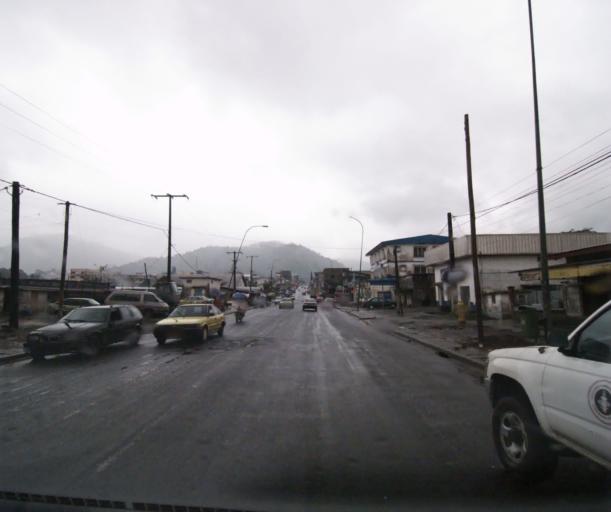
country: CM
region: South-West Province
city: Limbe
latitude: 4.0087
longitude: 9.2136
